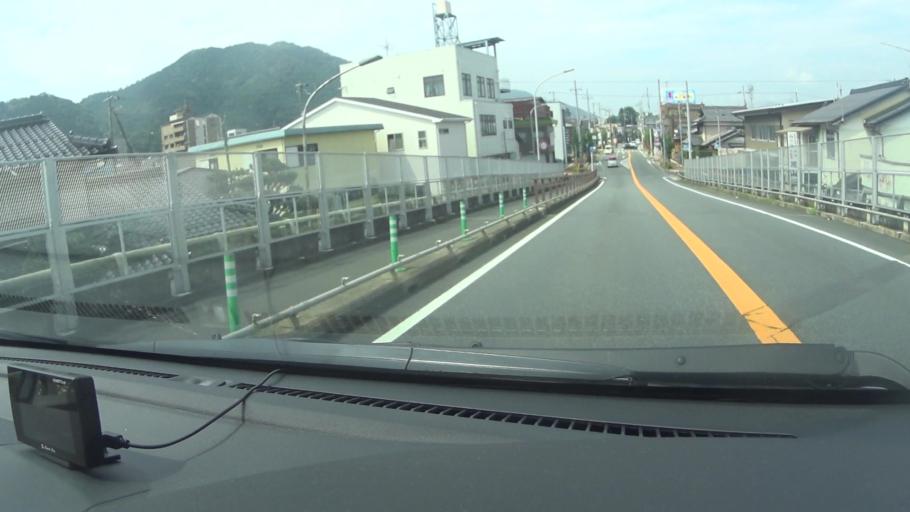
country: JP
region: Kyoto
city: Ayabe
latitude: 35.2999
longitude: 135.2586
